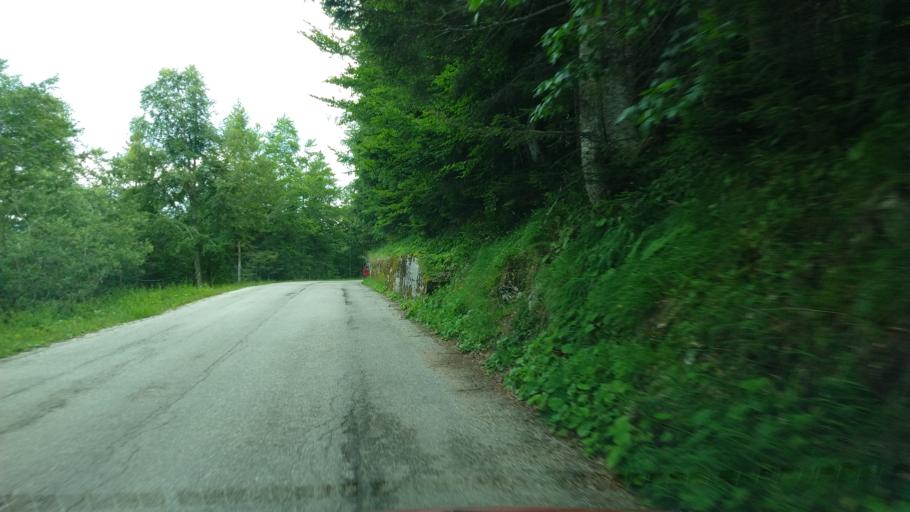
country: IT
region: Veneto
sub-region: Provincia di Vicenza
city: Lastebasse
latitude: 45.8938
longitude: 11.2721
